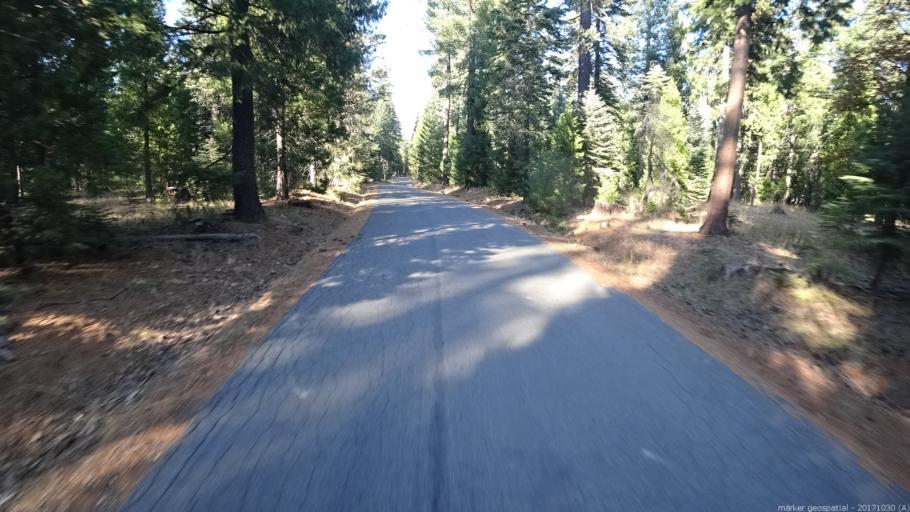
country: US
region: California
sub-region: Shasta County
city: Shingletown
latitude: 40.5475
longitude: -121.7340
